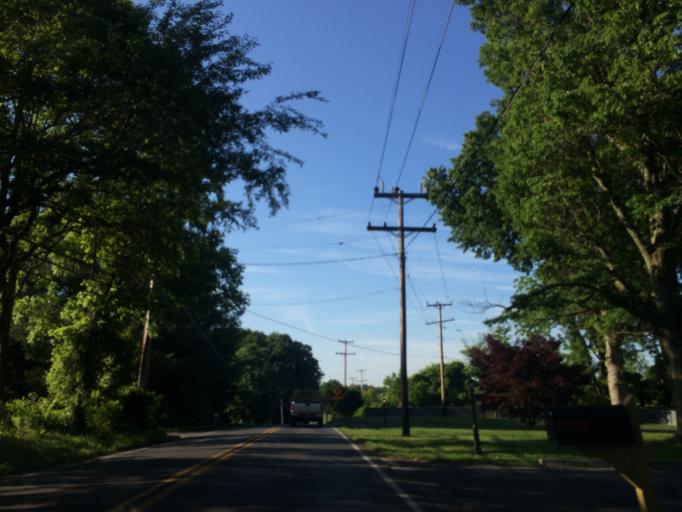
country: US
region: Maryland
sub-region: Howard County
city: Highland
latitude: 39.2323
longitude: -76.9386
